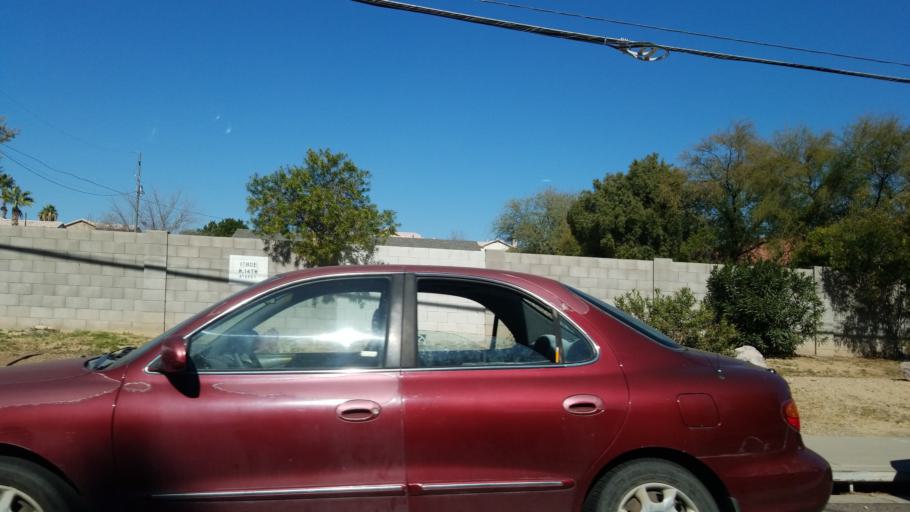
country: US
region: Arizona
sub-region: Maricopa County
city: Paradise Valley
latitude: 33.6477
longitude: -112.0523
